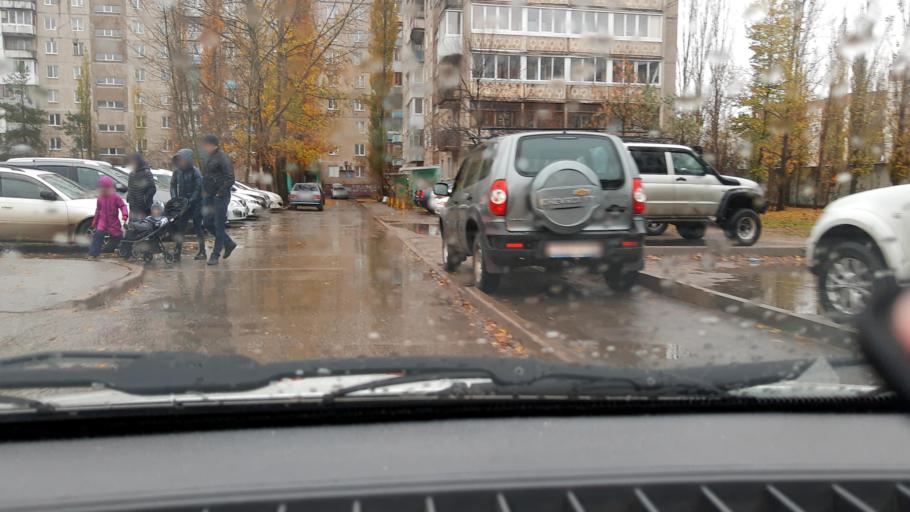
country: RU
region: Bashkortostan
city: Ufa
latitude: 54.7657
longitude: 56.0594
